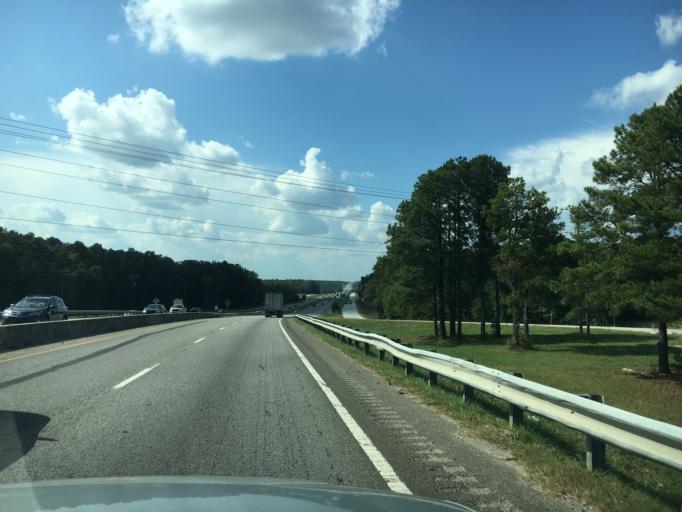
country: US
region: South Carolina
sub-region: Greenville County
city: Fountain Inn
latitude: 34.6689
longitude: -82.1825
